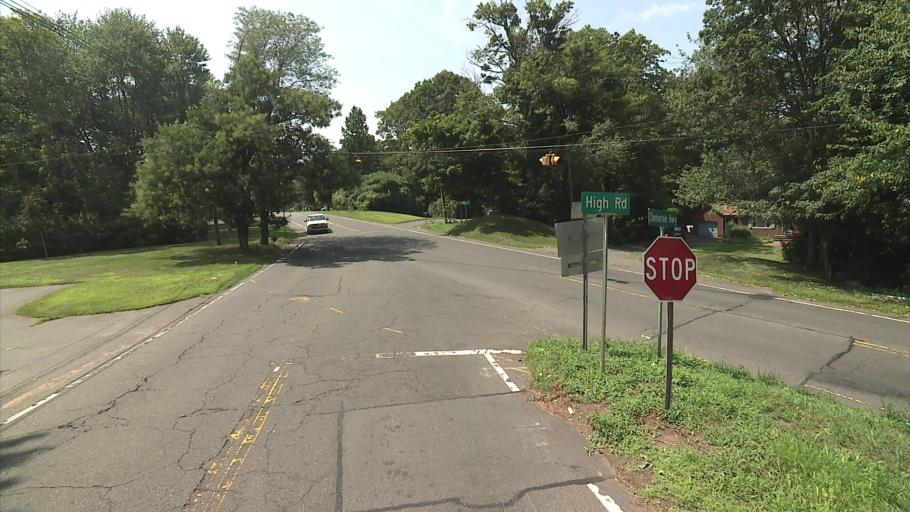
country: US
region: Connecticut
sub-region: Hartford County
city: Kensington
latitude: 41.6130
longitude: -72.7932
